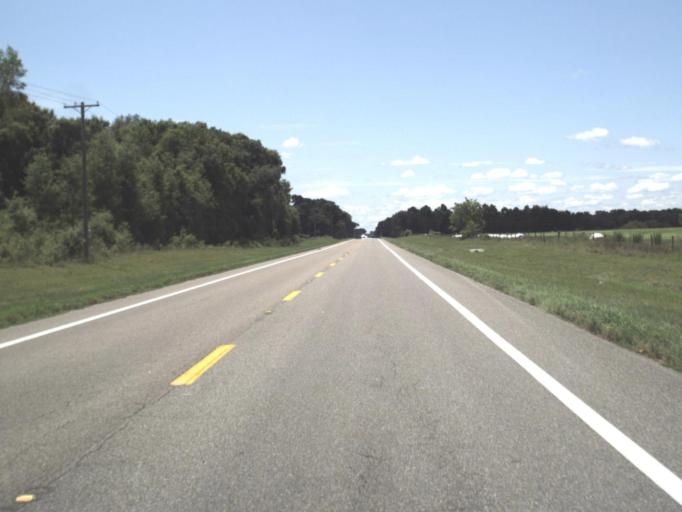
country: US
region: Florida
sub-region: Lafayette County
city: Mayo
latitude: 30.0286
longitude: -83.0572
